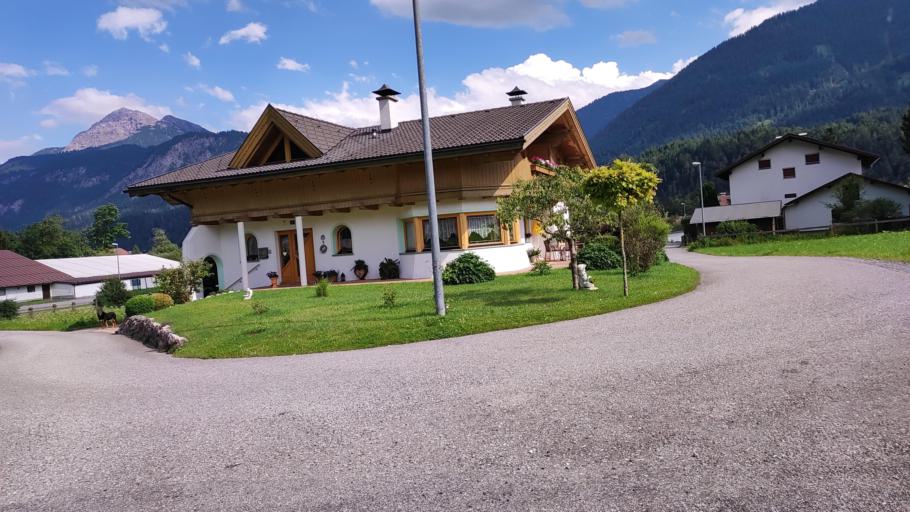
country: AT
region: Tyrol
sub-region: Politischer Bezirk Reutte
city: Nesselwangle
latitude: 47.4434
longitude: 10.6382
